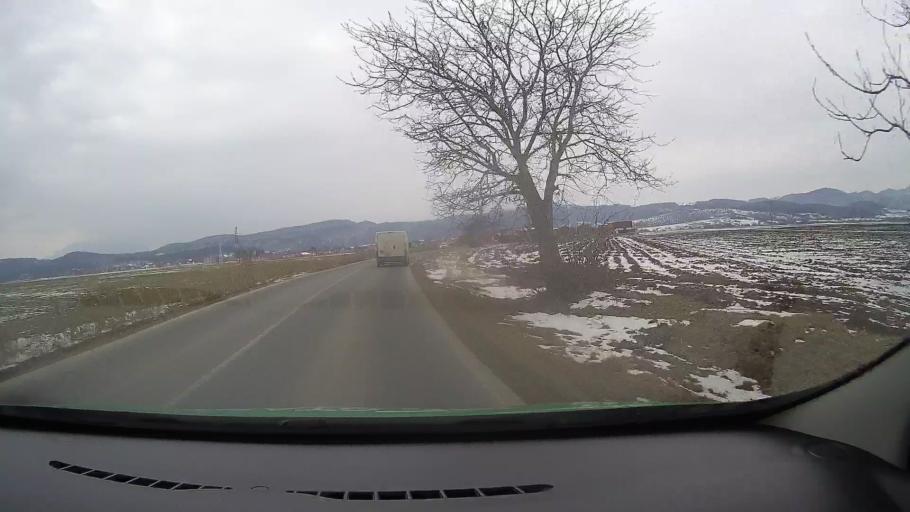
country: RO
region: Brasov
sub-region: Comuna Vulcan
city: Vulcan
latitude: 45.6361
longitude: 25.4372
